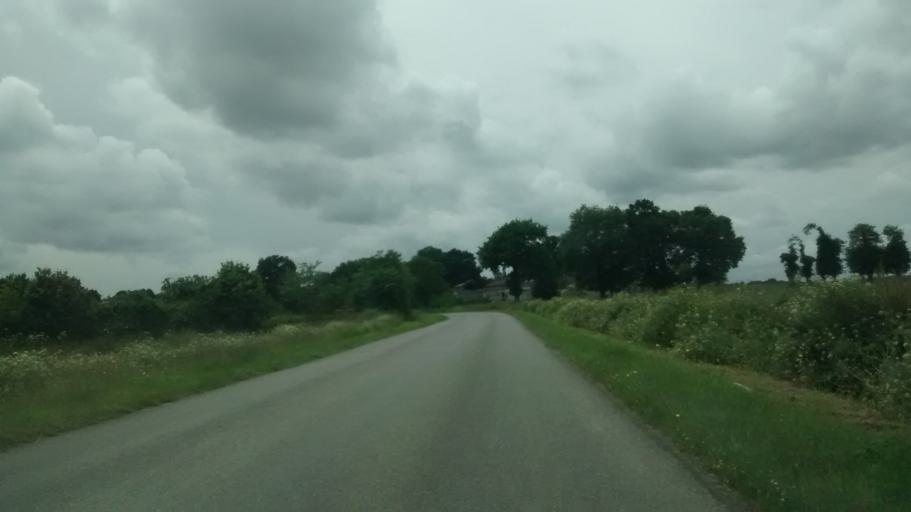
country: FR
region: Brittany
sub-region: Departement du Morbihan
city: Ruffiac
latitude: 47.8300
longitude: -2.2466
